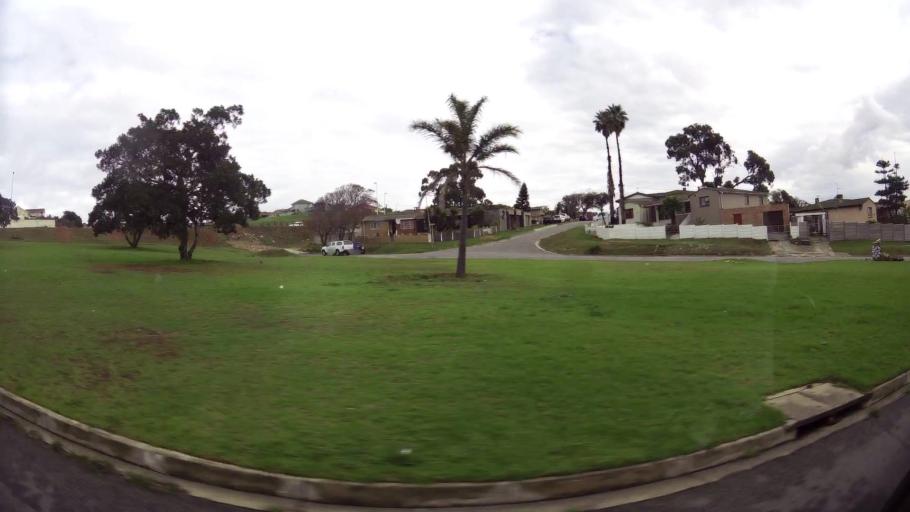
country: ZA
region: Eastern Cape
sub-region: Nelson Mandela Bay Metropolitan Municipality
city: Port Elizabeth
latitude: -33.9427
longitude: 25.5907
